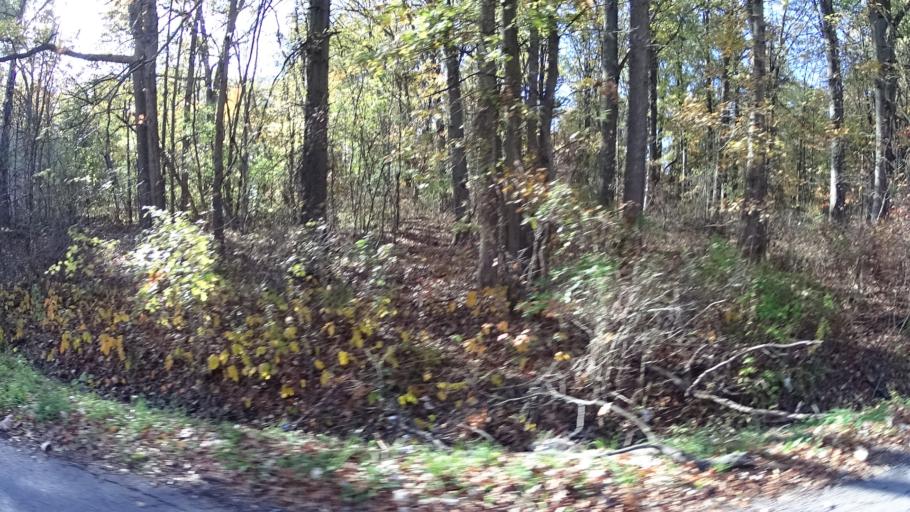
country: US
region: Ohio
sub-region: Lorain County
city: Lorain
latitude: 41.4351
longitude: -82.1411
